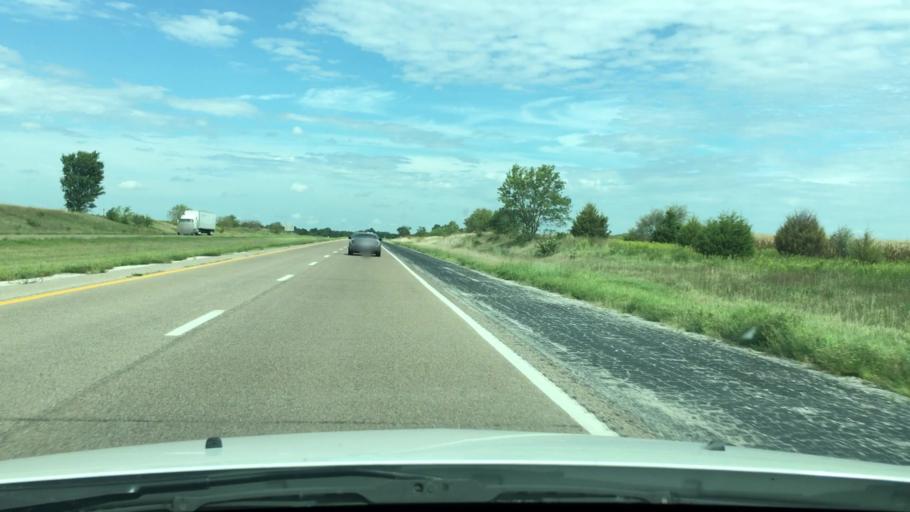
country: US
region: Missouri
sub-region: Audrain County
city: Mexico
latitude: 39.0313
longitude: -91.8867
